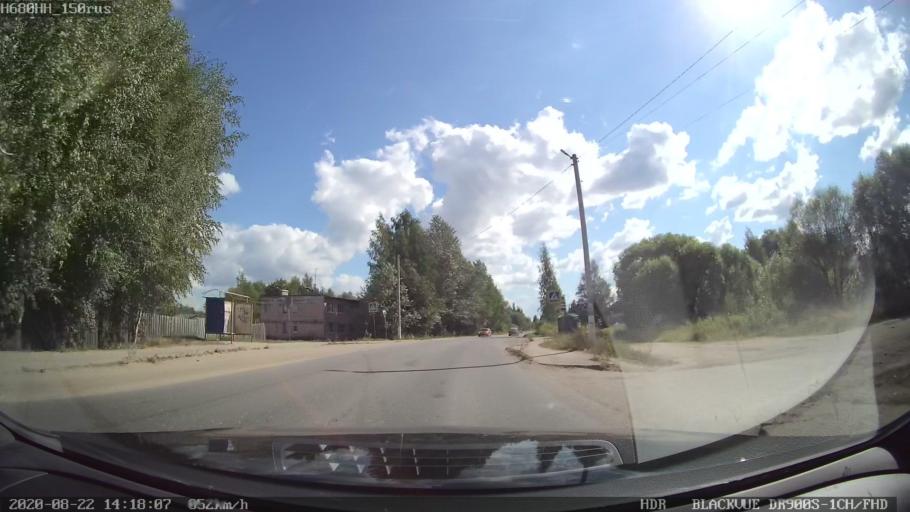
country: RU
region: Tverskaya
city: Bezhetsk
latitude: 57.7646
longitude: 36.7103
